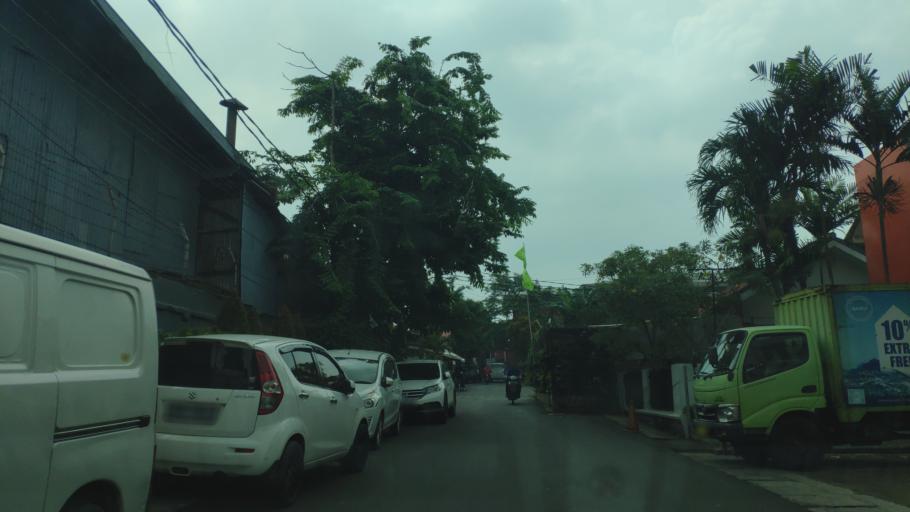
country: ID
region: Jakarta Raya
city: Jakarta
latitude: -6.2095
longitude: 106.7943
